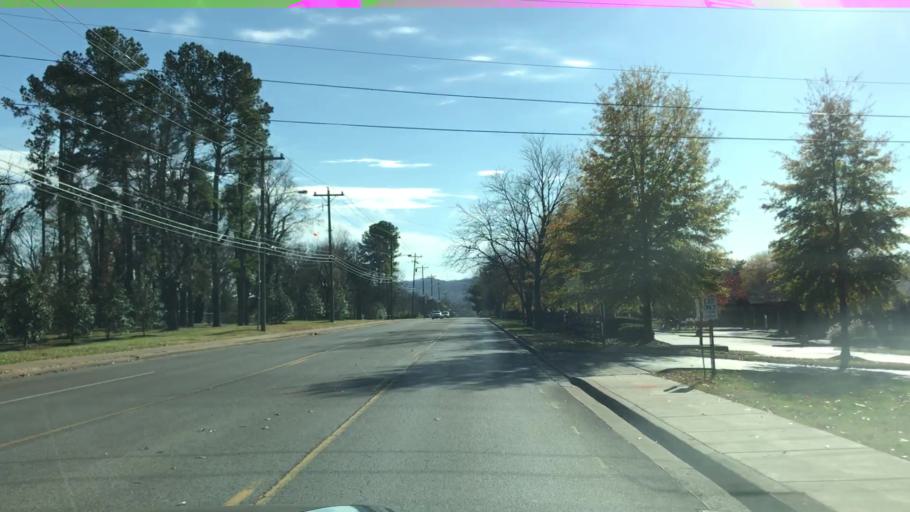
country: US
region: Tennessee
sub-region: Williamson County
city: Brentwood
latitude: 36.0340
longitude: -86.8173
